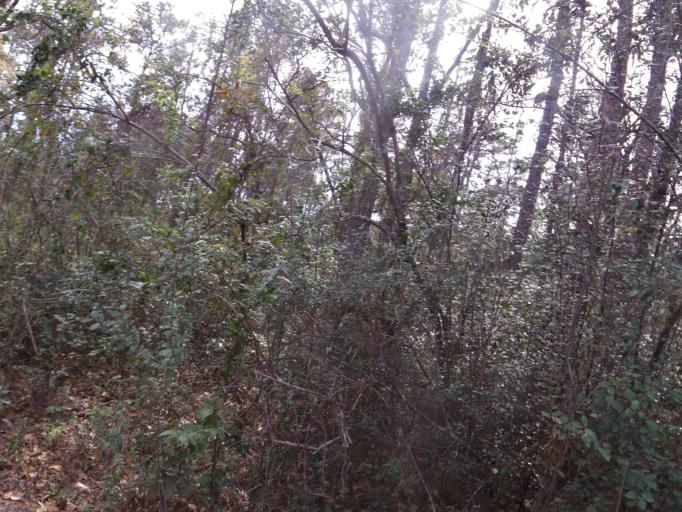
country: US
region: Florida
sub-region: Clay County
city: Middleburg
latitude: 30.1274
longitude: -81.8934
